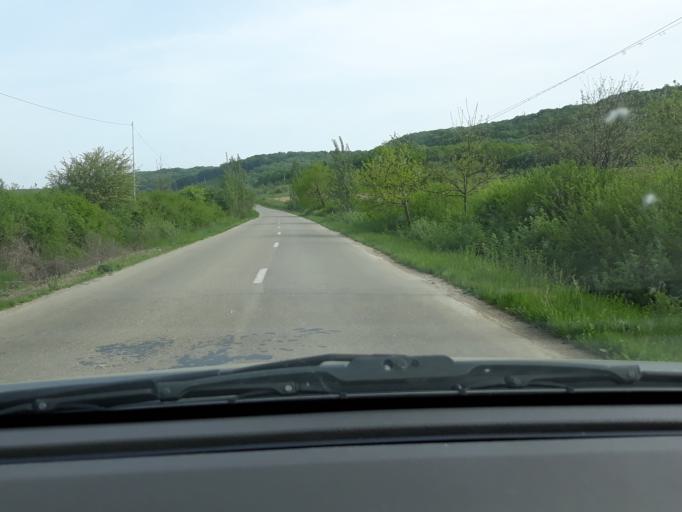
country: RO
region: Bihor
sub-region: Comuna Sanmartin
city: Sanmartin
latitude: 46.9805
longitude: 22.0011
